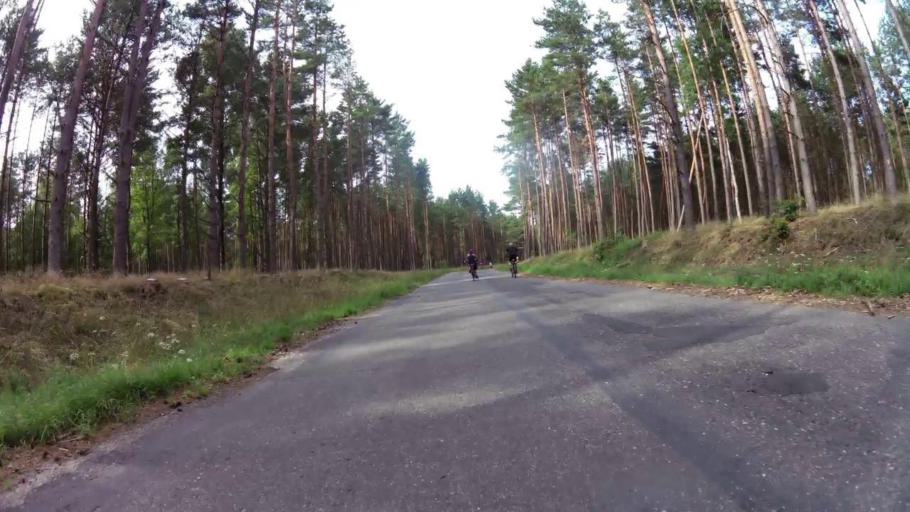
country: PL
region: West Pomeranian Voivodeship
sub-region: Powiat stargardzki
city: Insko
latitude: 53.4156
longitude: 15.6023
